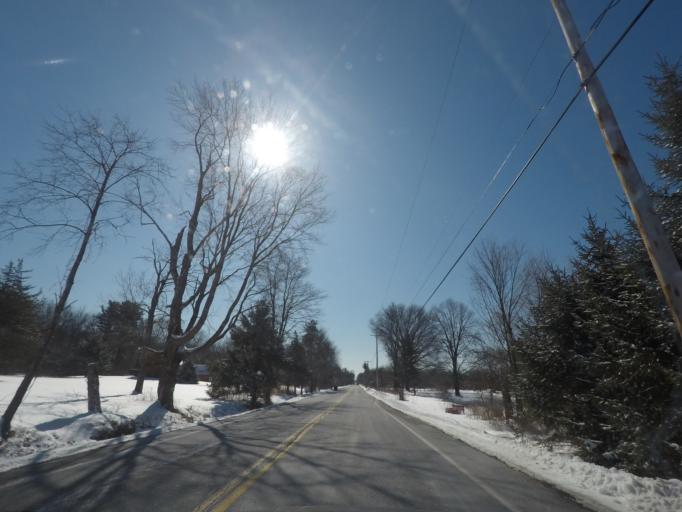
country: US
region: New York
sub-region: Saratoga County
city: Ballston Spa
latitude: 42.9838
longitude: -73.8328
